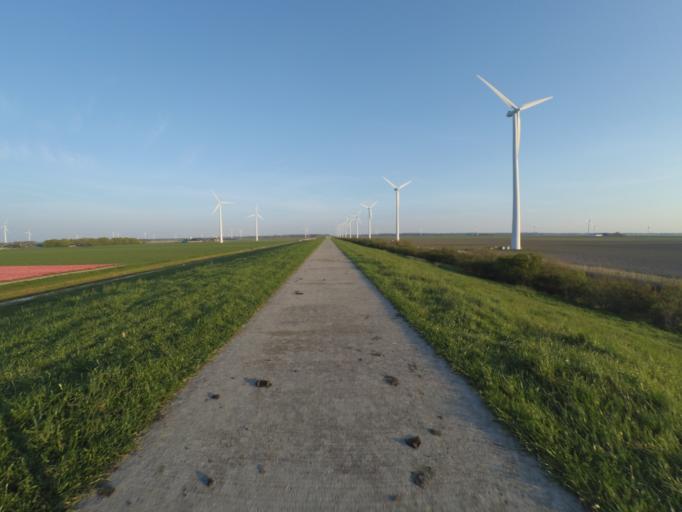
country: NL
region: Flevoland
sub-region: Gemeente Zeewolde
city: Zeewolde
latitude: 52.3852
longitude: 5.5327
